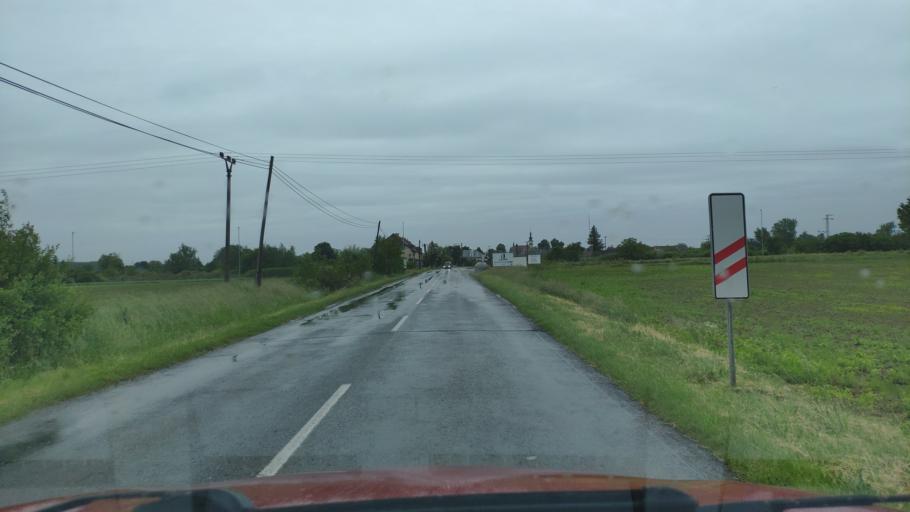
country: SK
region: Kosicky
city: Cierna nad Tisou
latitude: 48.4177
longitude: 22.0272
